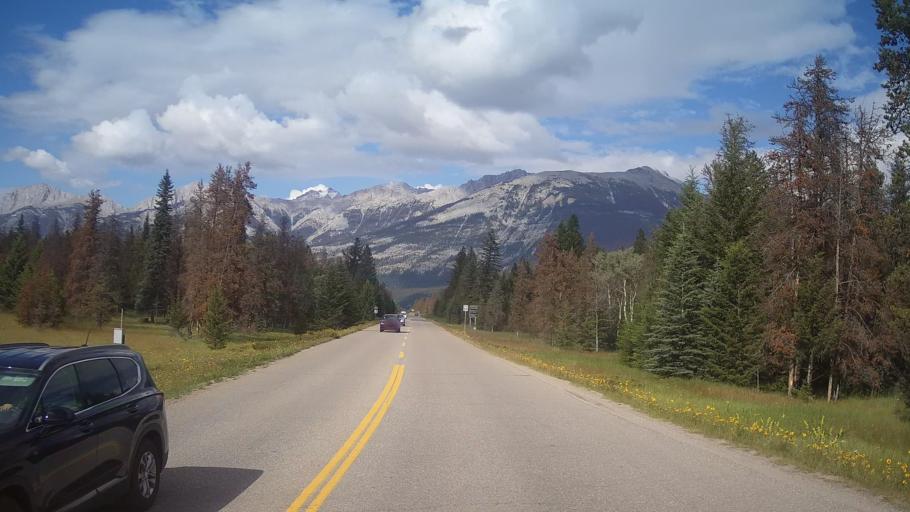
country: CA
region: Alberta
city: Jasper Park Lodge
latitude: 52.9097
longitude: -118.0548
